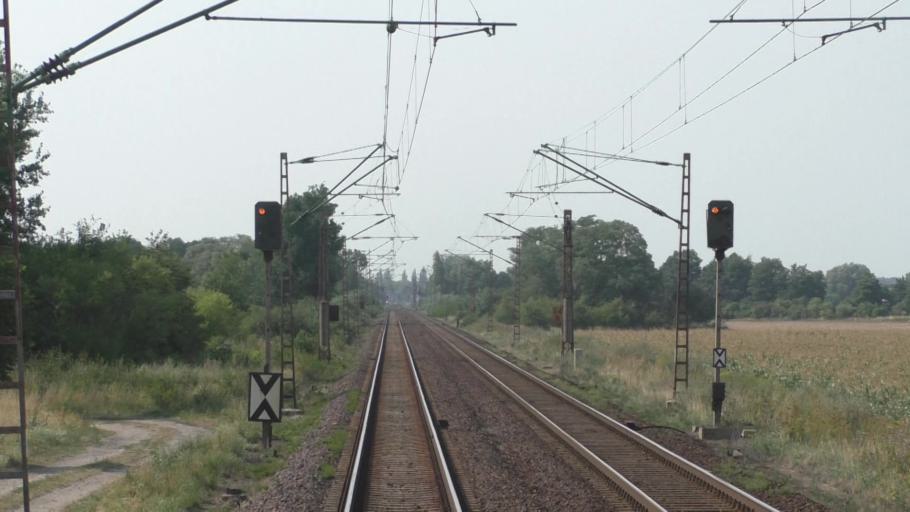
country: DE
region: Saxony-Anhalt
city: Gommern
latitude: 52.0650
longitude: 11.8586
